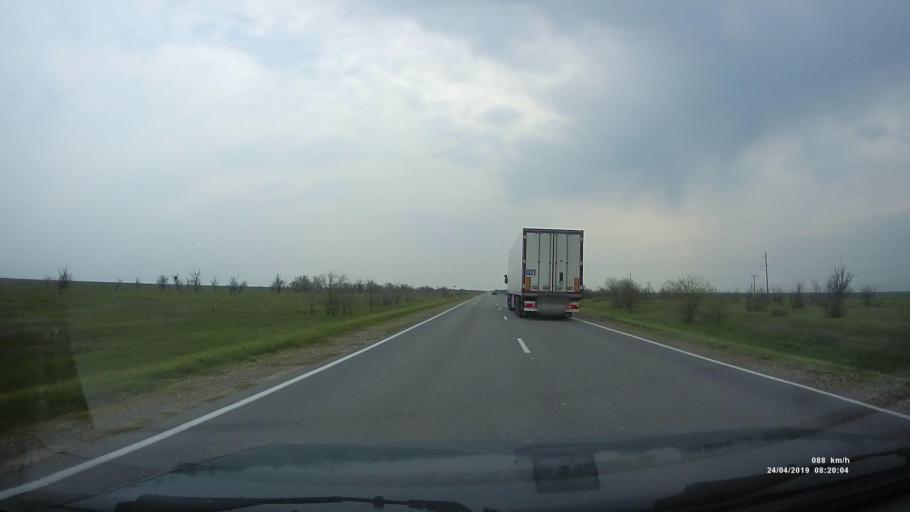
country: RU
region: Kalmykiya
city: Priyutnoye
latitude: 46.1061
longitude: 43.6761
